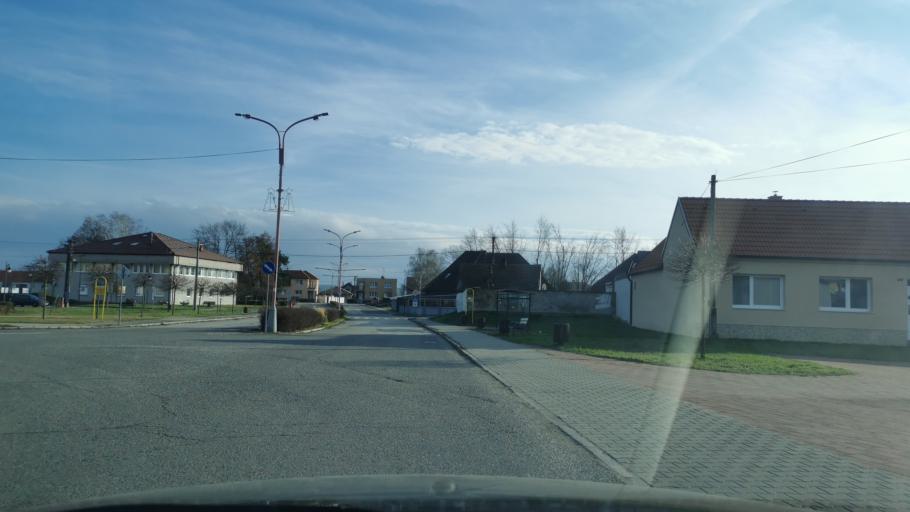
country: SK
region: Trnavsky
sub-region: Okres Skalica
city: Holic
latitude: 48.7882
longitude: 17.1160
